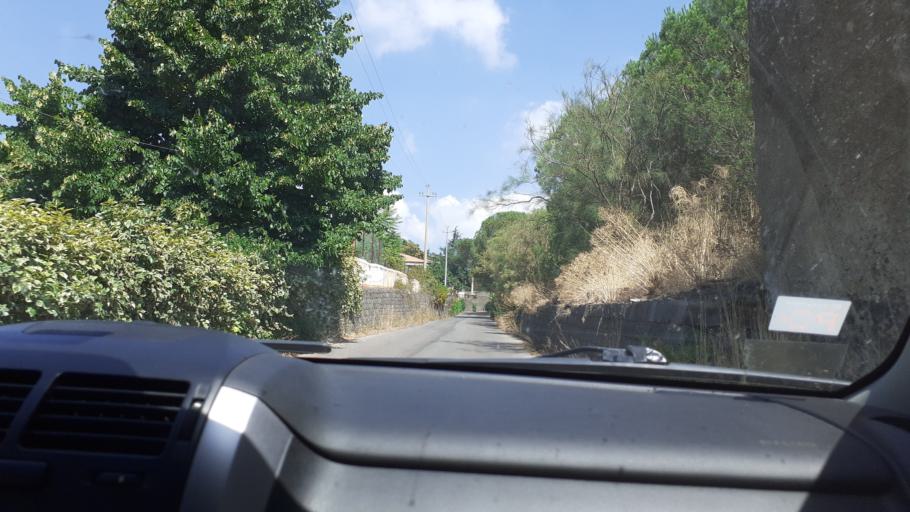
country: IT
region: Sicily
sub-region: Catania
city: Nicolosi
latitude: 37.6277
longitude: 15.0246
